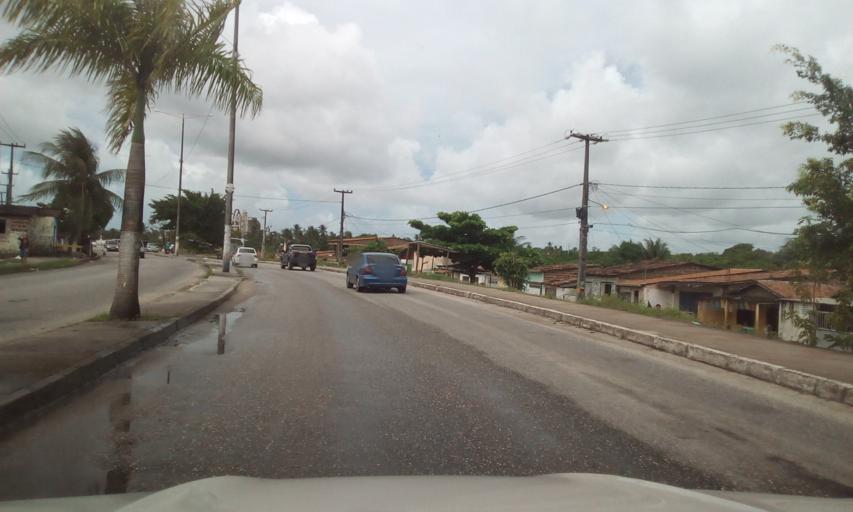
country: BR
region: Paraiba
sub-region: Bayeux
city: Bayeux
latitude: -7.1214
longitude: -34.9038
